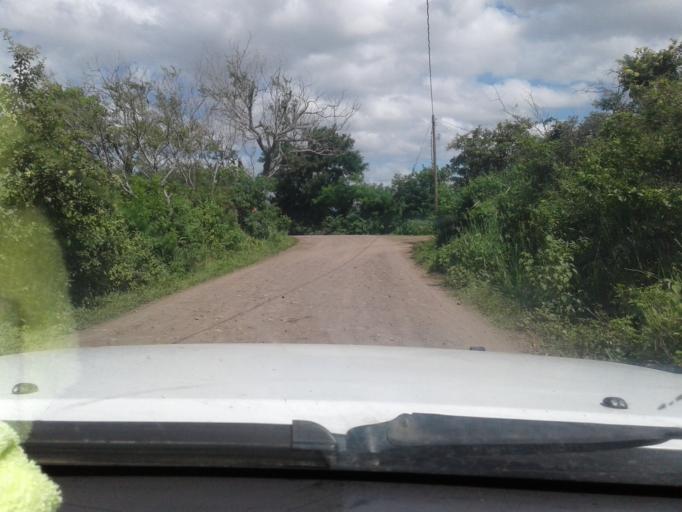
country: NI
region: Matagalpa
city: Ciudad Dario
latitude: 12.8418
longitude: -86.1086
